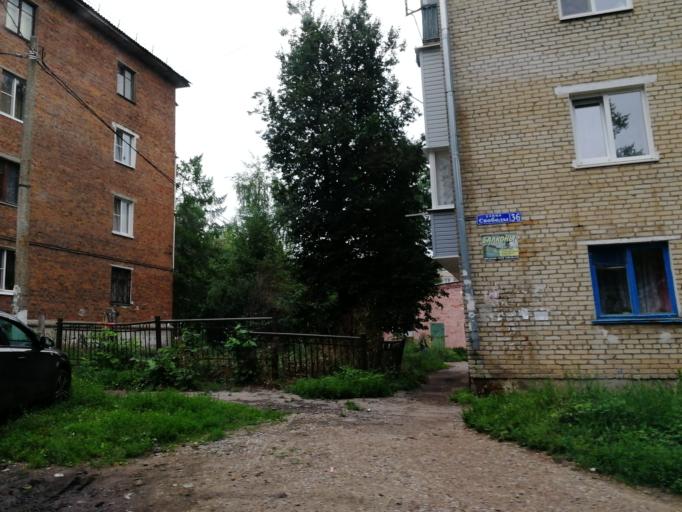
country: RU
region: Tula
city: Bogoroditsk
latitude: 53.7685
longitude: 38.1264
